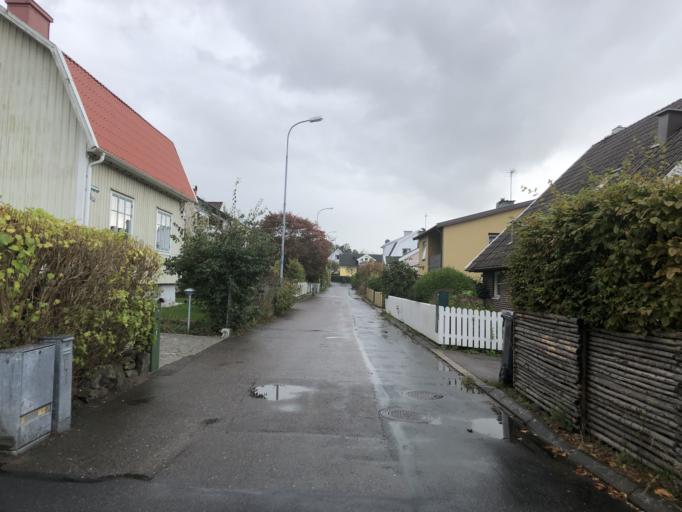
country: SE
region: Vaestra Goetaland
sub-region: Molndal
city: Moelndal
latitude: 57.6538
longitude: 12.0349
